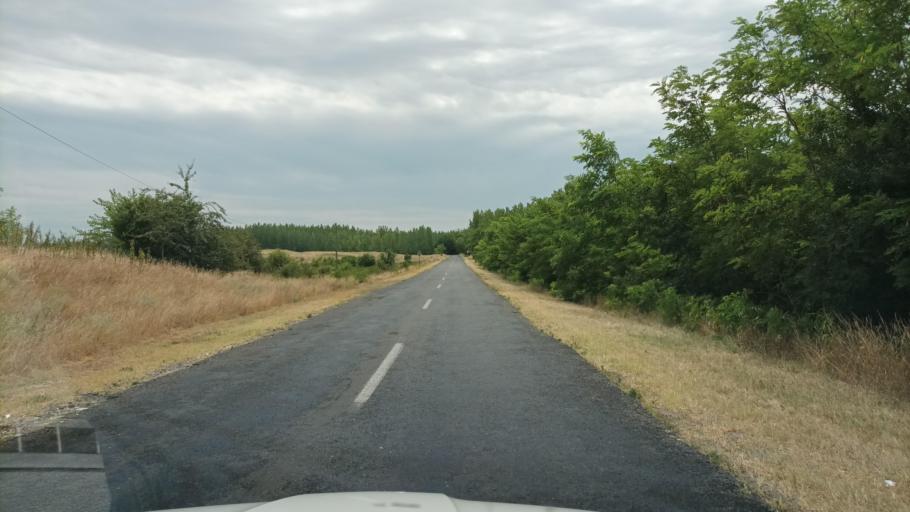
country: HU
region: Pest
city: Orkeny
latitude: 47.1085
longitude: 19.3597
